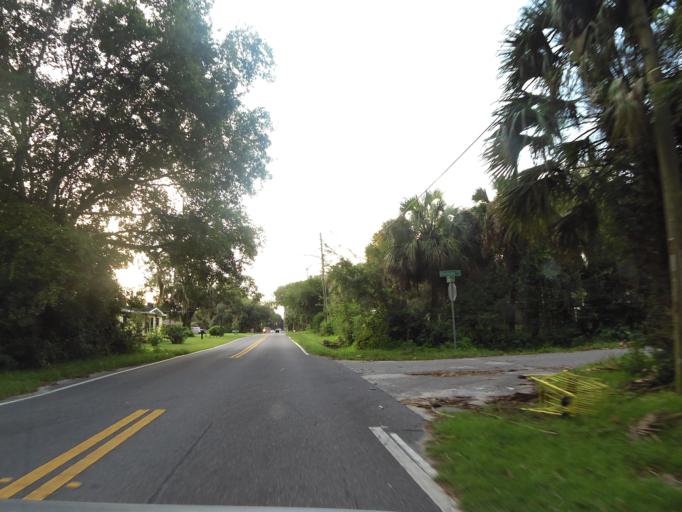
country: US
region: Florida
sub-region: Duval County
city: Jacksonville
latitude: 30.3256
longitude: -81.7838
